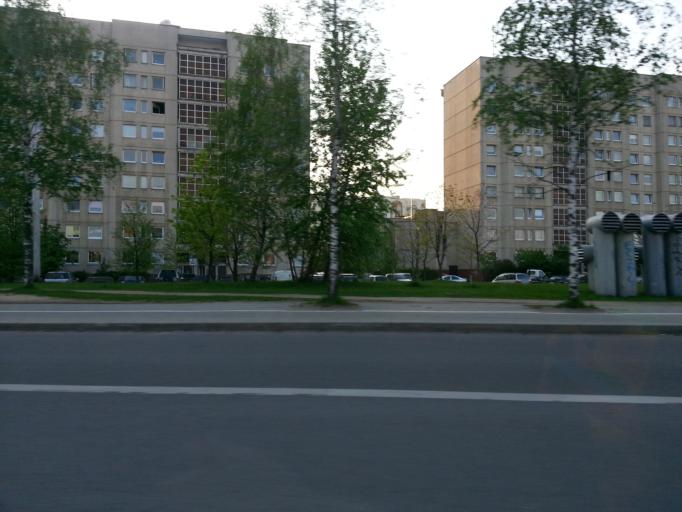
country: LT
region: Vilnius County
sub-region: Vilnius
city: Fabijoniskes
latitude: 54.7290
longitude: 25.2356
